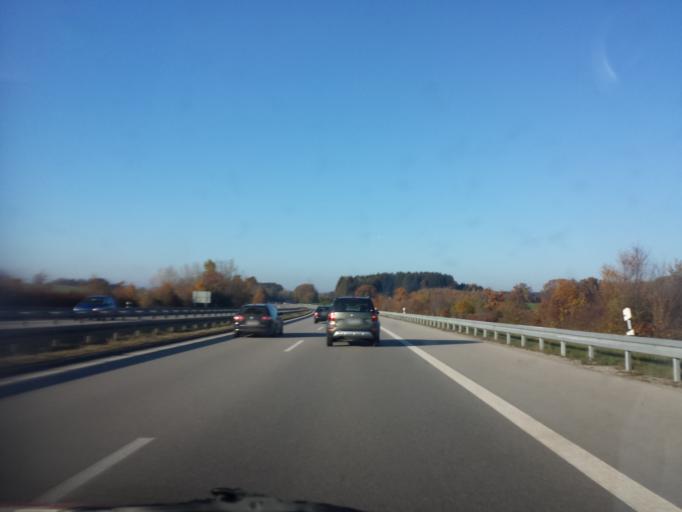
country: DE
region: Bavaria
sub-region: Upper Bavaria
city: Antdorf
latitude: 47.7445
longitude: 11.3319
